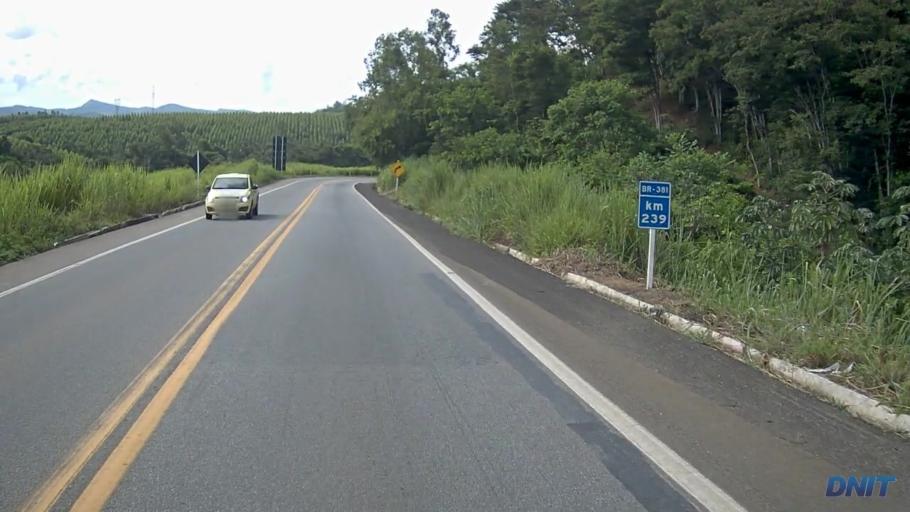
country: BR
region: Minas Gerais
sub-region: Ipaba
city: Ipaba
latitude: -19.3771
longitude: -42.4615
